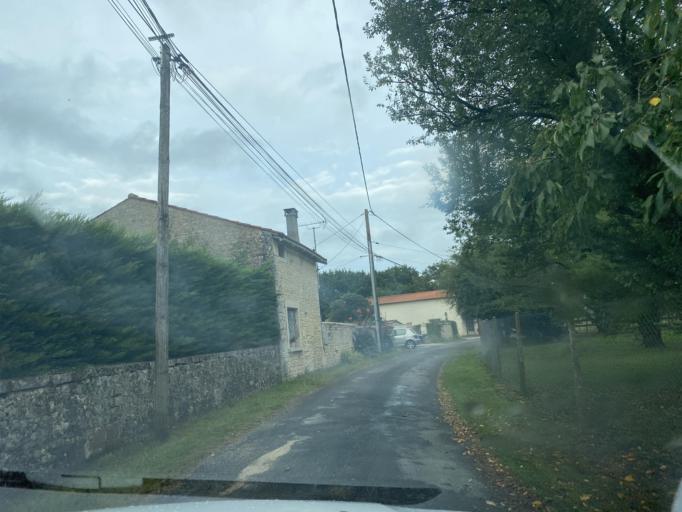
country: FR
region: Poitou-Charentes
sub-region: Departement de la Charente-Maritime
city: Gemozac
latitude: 45.5421
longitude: -0.6525
